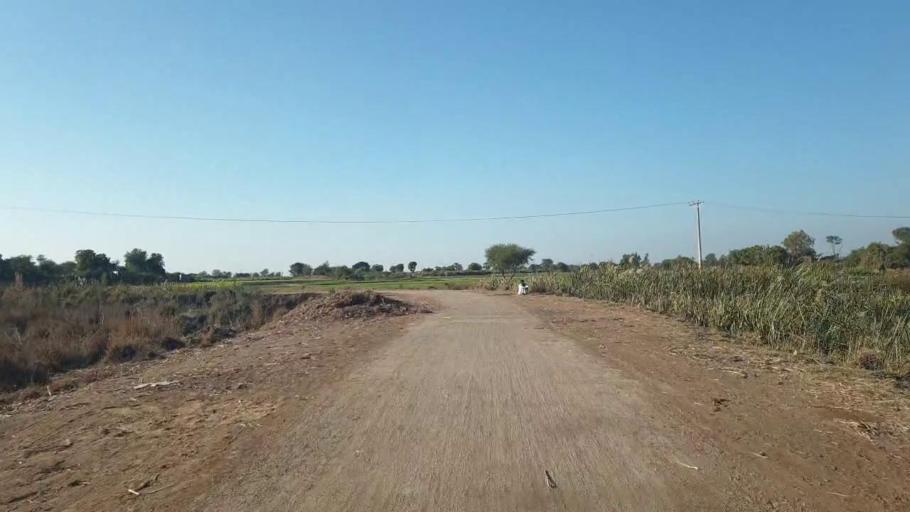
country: PK
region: Sindh
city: Shahdadpur
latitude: 25.9291
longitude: 68.5941
